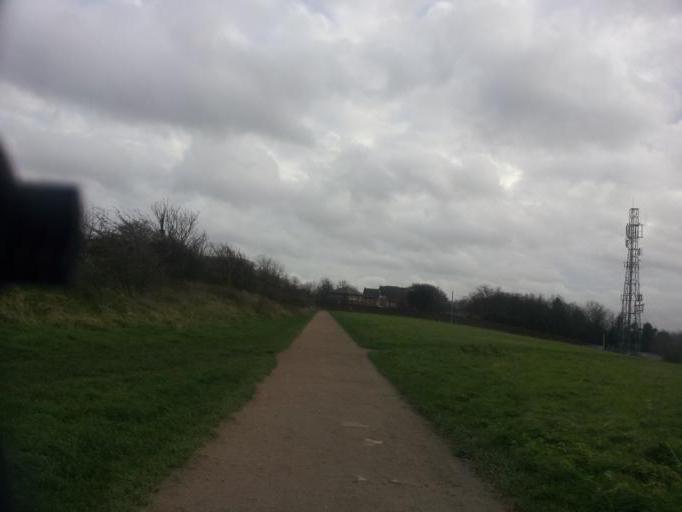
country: GB
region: England
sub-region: Kent
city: Chatham
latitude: 51.3806
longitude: 0.5366
